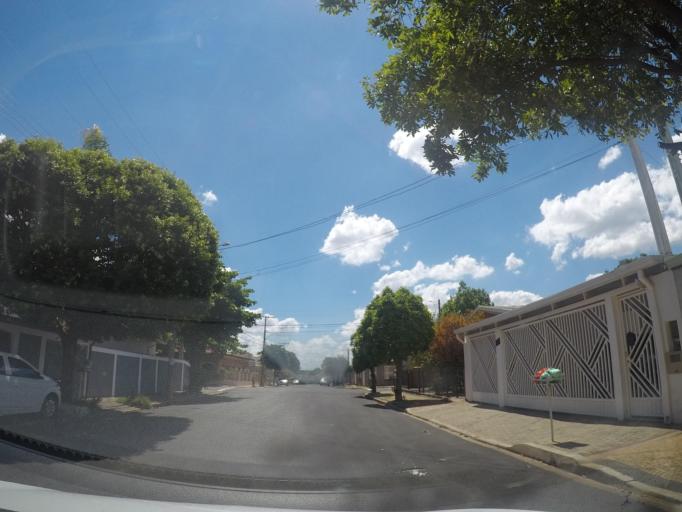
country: BR
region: Sao Paulo
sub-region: Sumare
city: Sumare
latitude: -22.8243
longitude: -47.2731
